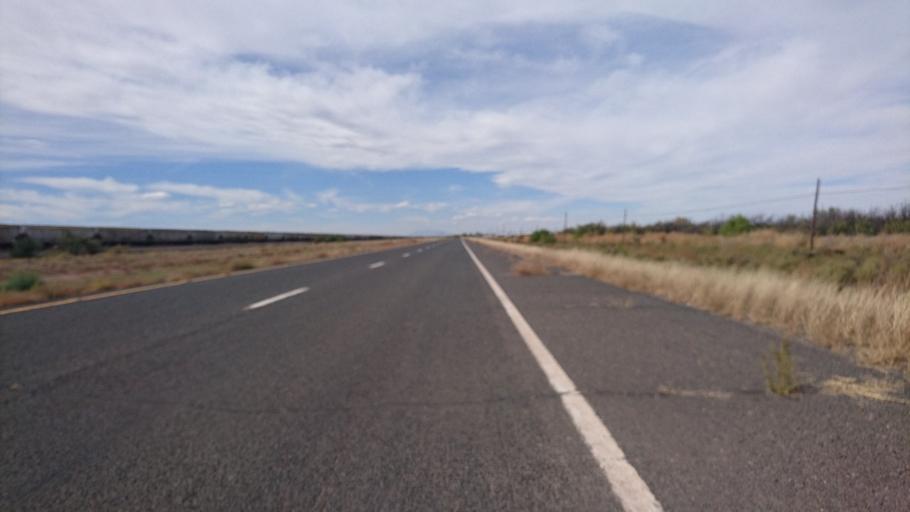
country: US
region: Arizona
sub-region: Navajo County
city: Winslow
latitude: 35.0094
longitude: -110.6642
